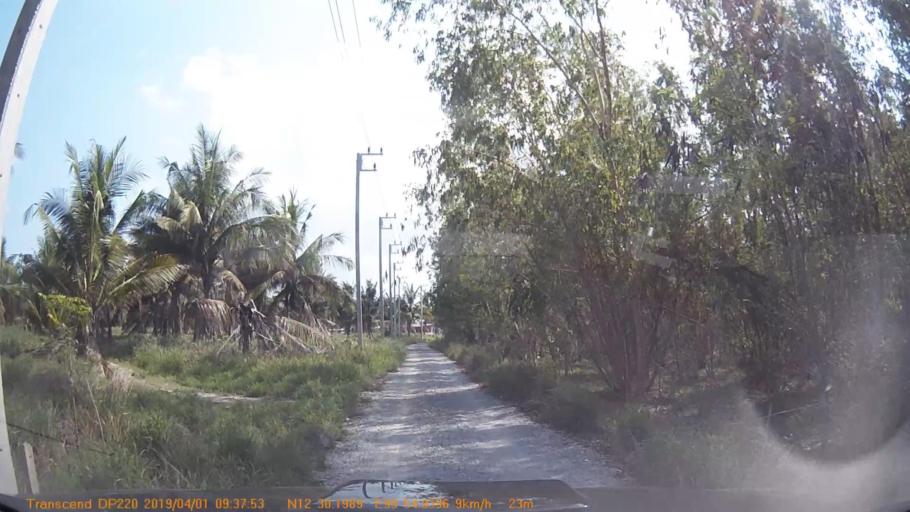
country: TH
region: Prachuap Khiri Khan
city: Hua Hin
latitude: 12.5034
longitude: 99.9157
